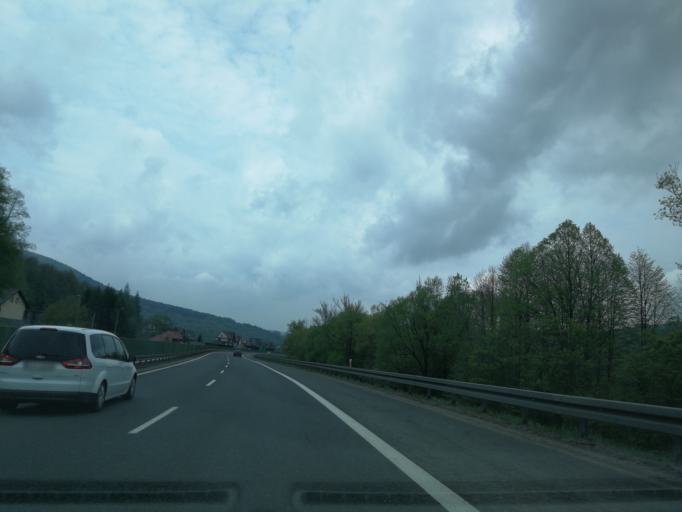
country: PL
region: Lesser Poland Voivodeship
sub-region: Powiat myslenicki
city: Pcim
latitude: 49.7546
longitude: 19.9699
